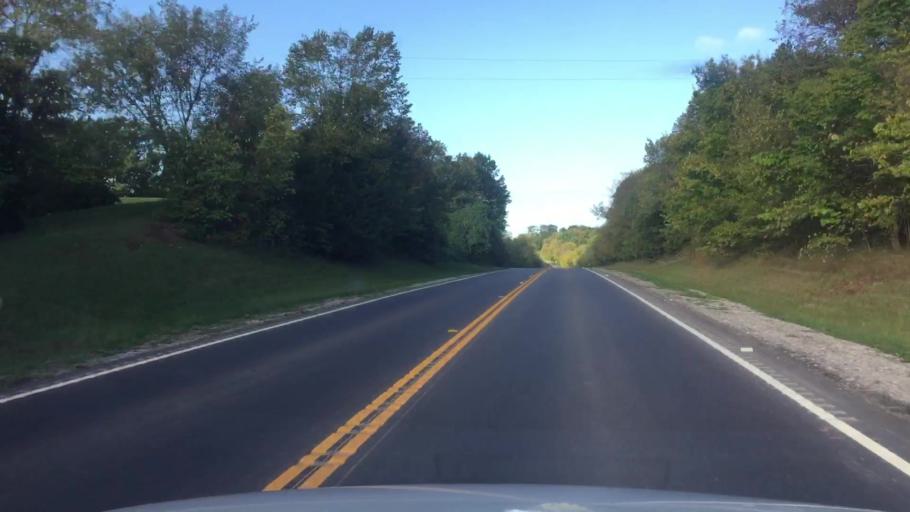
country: US
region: Missouri
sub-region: Howard County
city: New Franklin
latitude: 38.9974
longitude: -92.5910
